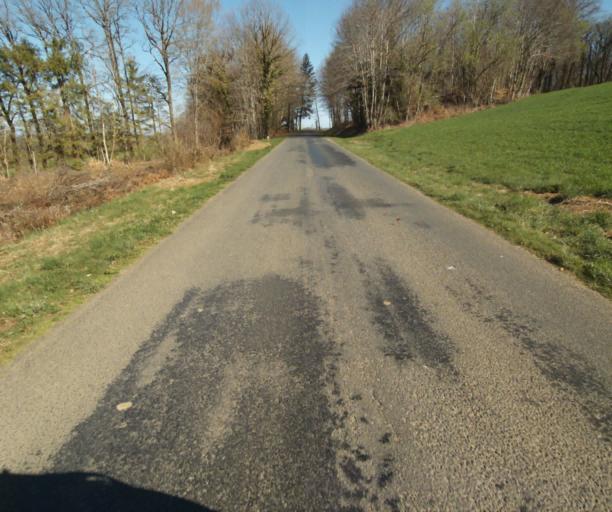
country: FR
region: Limousin
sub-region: Departement de la Correze
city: Seilhac
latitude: 45.3977
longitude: 1.7477
